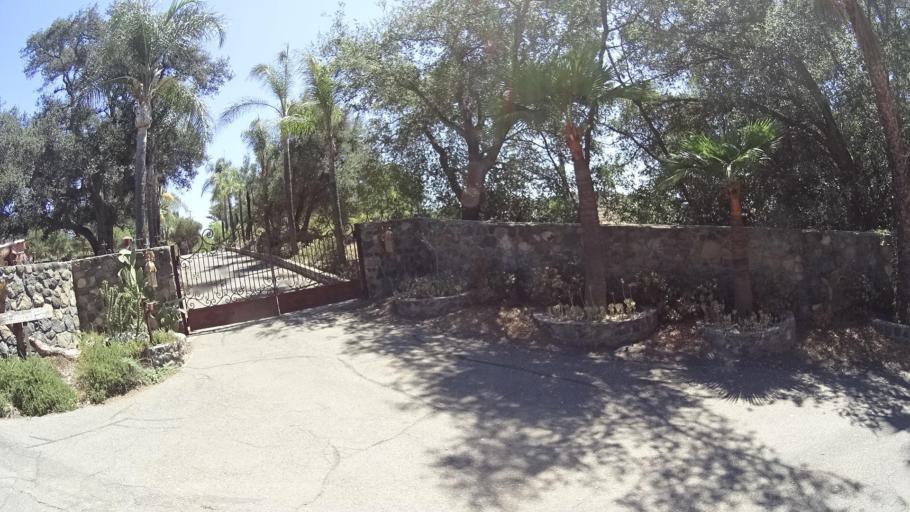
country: US
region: California
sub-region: San Diego County
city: Rainbow
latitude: 33.3956
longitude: -117.0347
